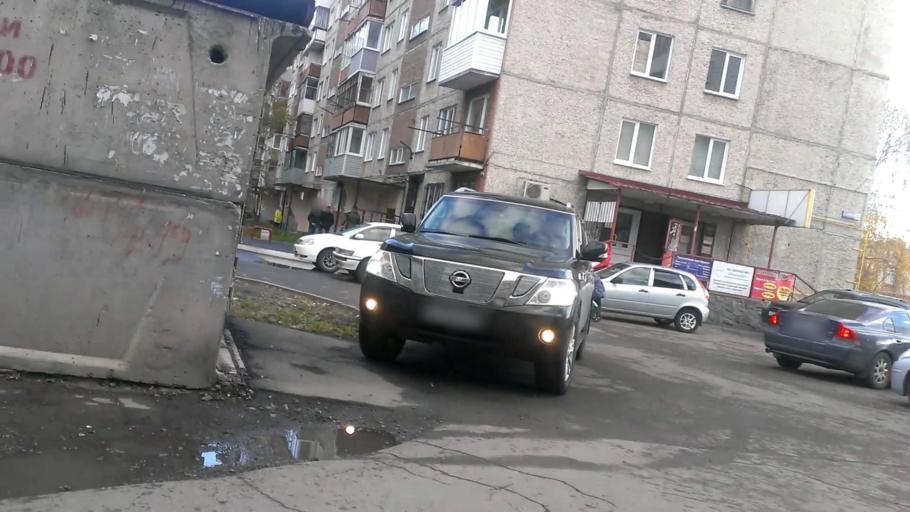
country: RU
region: Altai Krai
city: Novosilikatnyy
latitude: 53.3566
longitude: 83.6759
